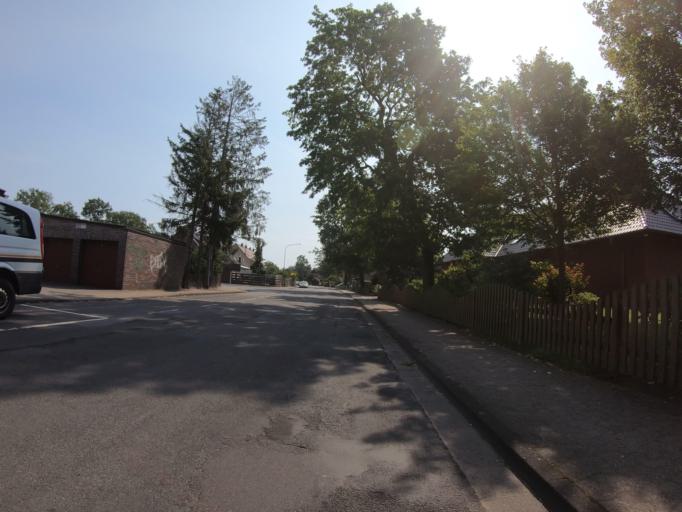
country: DE
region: Lower Saxony
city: Gifhorn
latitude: 52.4690
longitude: 10.5593
